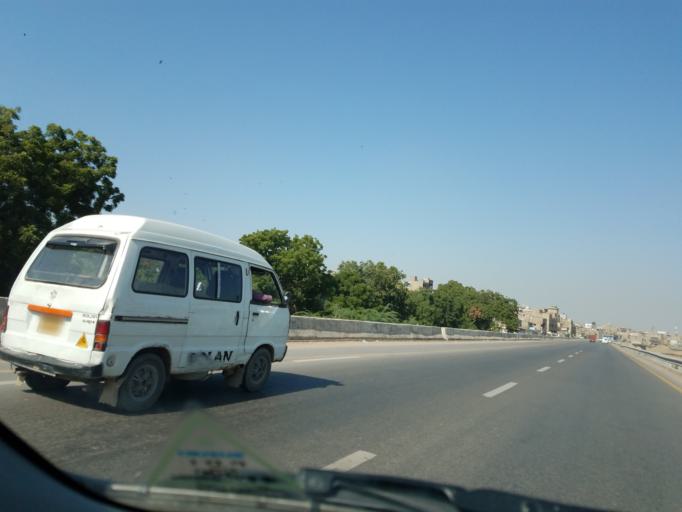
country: PK
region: Sindh
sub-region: Karachi District
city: Karachi
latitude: 24.8866
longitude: 67.0234
